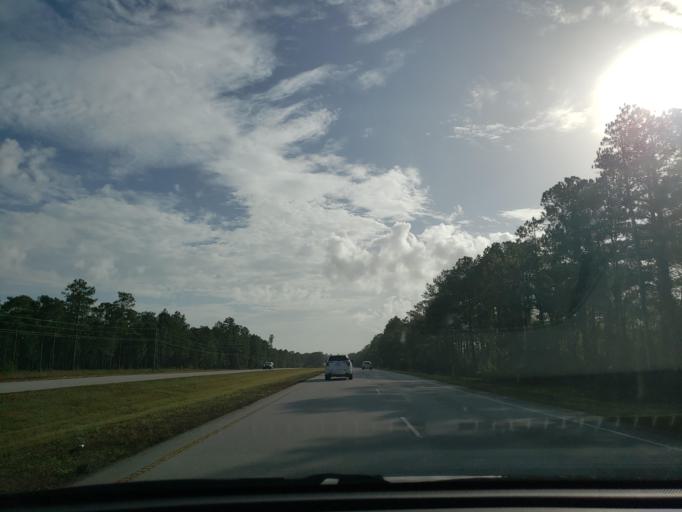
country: US
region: North Carolina
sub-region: Onslow County
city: Sneads Ferry
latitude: 34.6245
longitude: -77.4828
